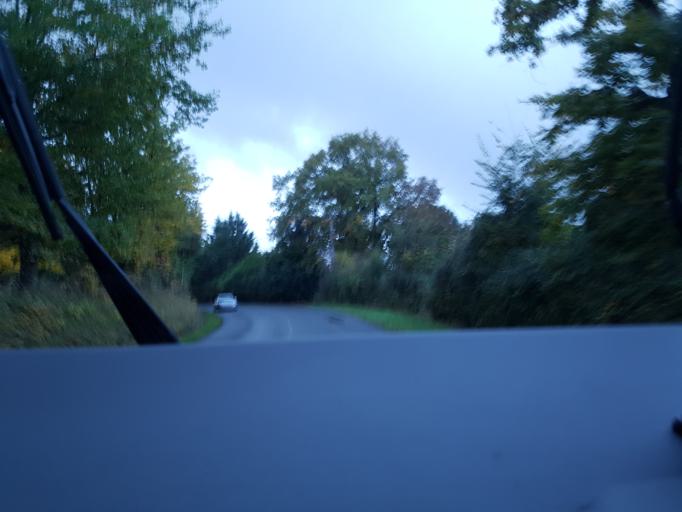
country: FR
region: Poitou-Charentes
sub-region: Departement des Deux-Sevres
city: Lezay
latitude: 46.2486
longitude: -0.0199
